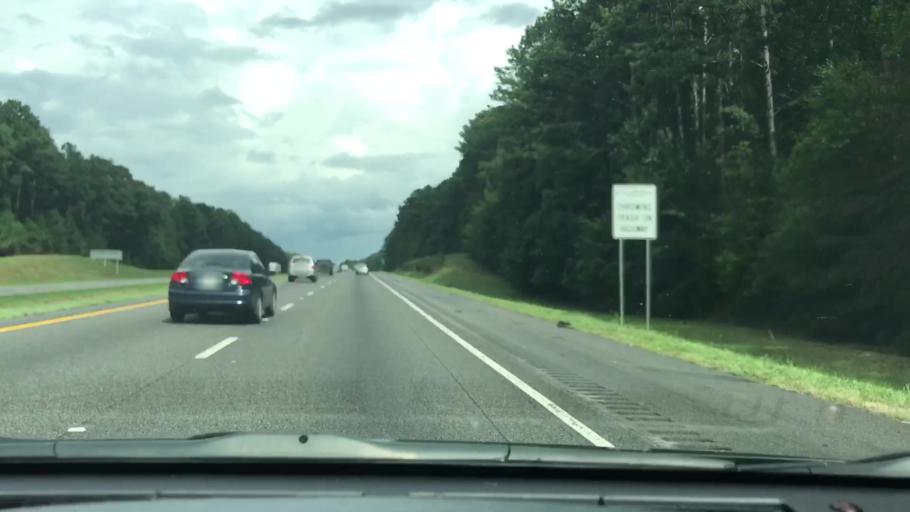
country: US
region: Georgia
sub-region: Newton County
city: Covington
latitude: 33.6104
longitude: -83.8003
